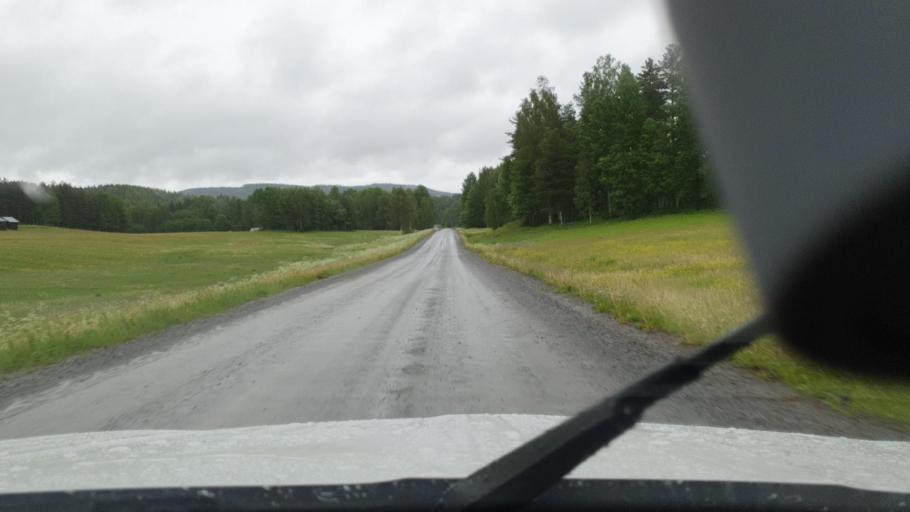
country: SE
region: Vaesterbotten
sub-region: Skelleftea Kommun
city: Burtraesk
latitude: 64.3668
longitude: 20.4015
